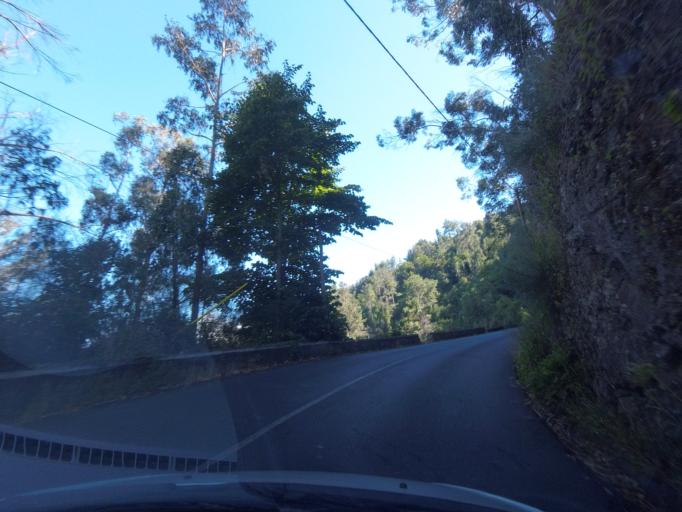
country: PT
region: Madeira
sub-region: Santa Cruz
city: Camacha
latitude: 32.6911
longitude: -16.8524
